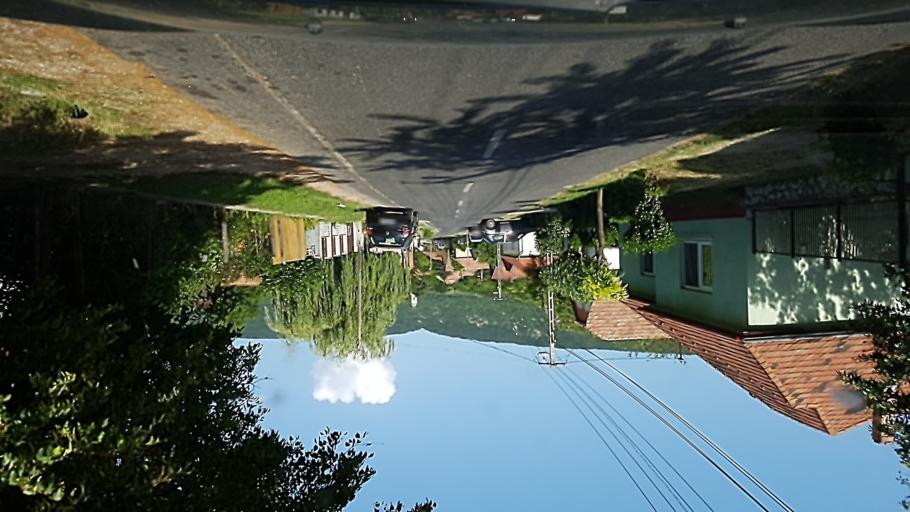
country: HU
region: Komarom-Esztergom
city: Kesztolc
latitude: 47.7110
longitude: 18.7924
